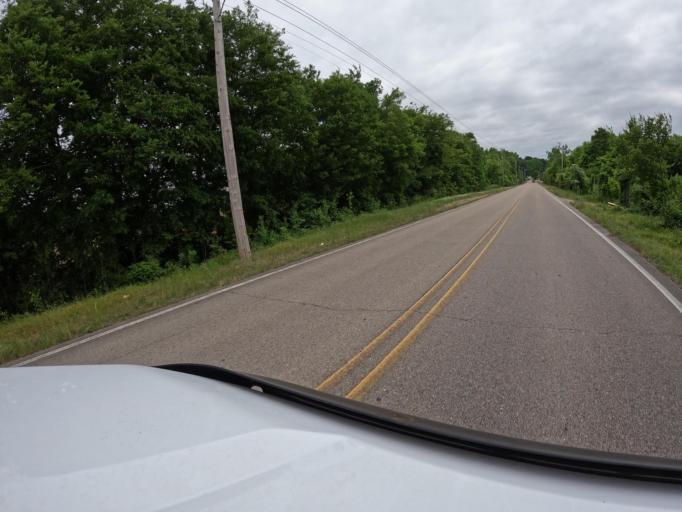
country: US
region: Mississippi
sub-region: Lee County
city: Tupelo
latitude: 34.2754
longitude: -88.7360
